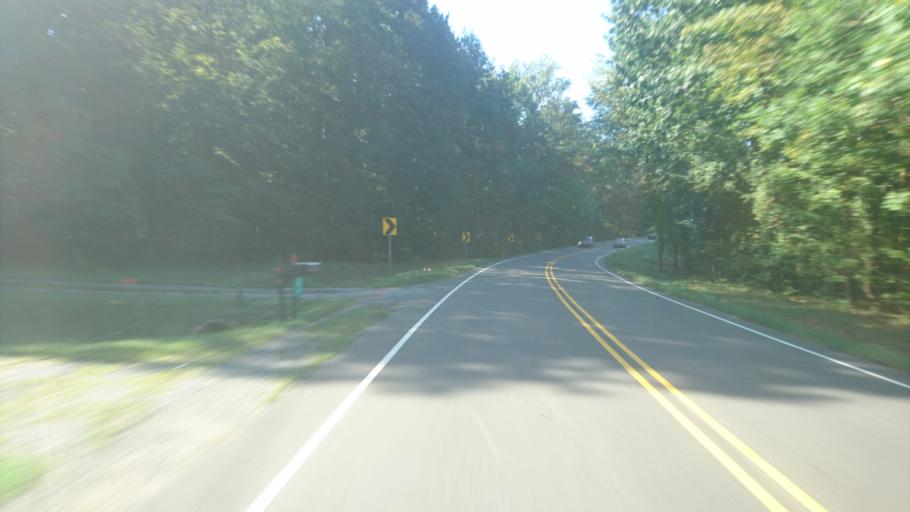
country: US
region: North Carolina
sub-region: Orange County
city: Hillsborough
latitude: 36.0019
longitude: -79.0664
